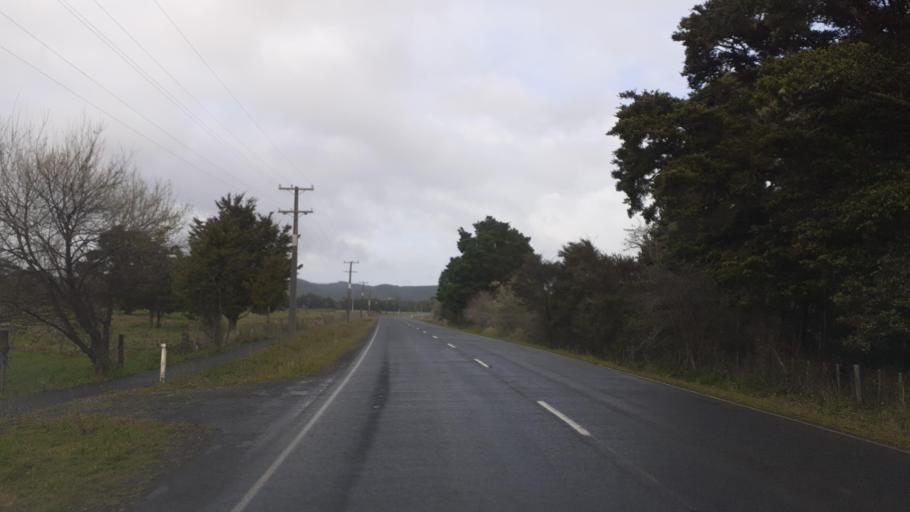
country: NZ
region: Northland
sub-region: Far North District
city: Moerewa
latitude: -35.3988
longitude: 173.9939
